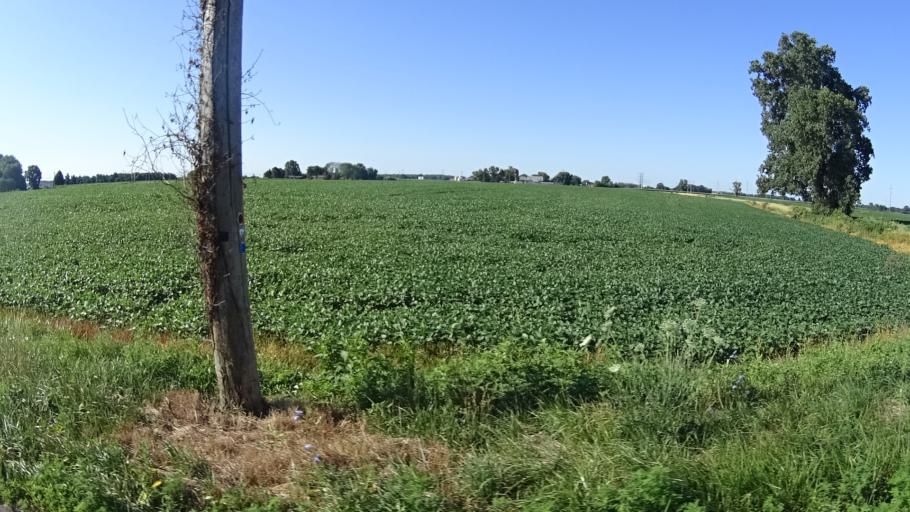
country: US
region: Ohio
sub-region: Erie County
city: Sandusky
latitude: 41.3971
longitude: -82.7360
